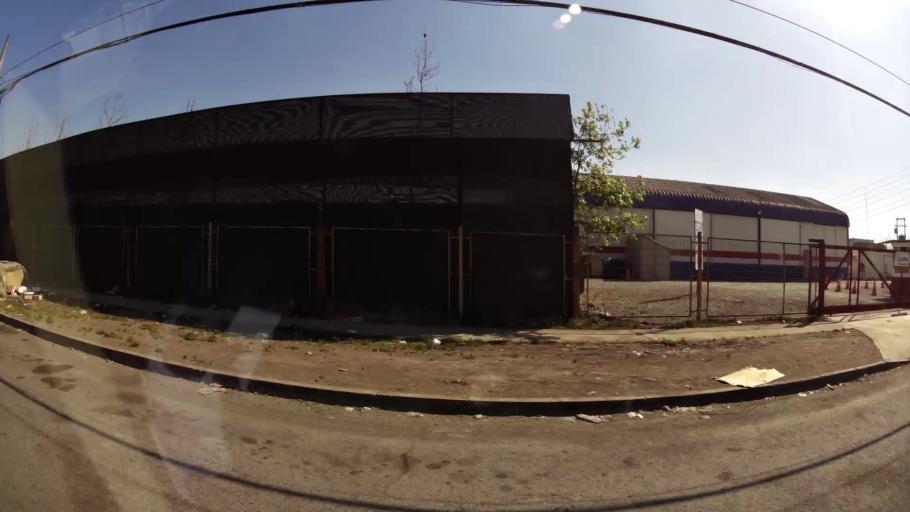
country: CL
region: Santiago Metropolitan
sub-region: Provincia de Chacabuco
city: Chicureo Abajo
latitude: -33.3323
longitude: -70.7058
